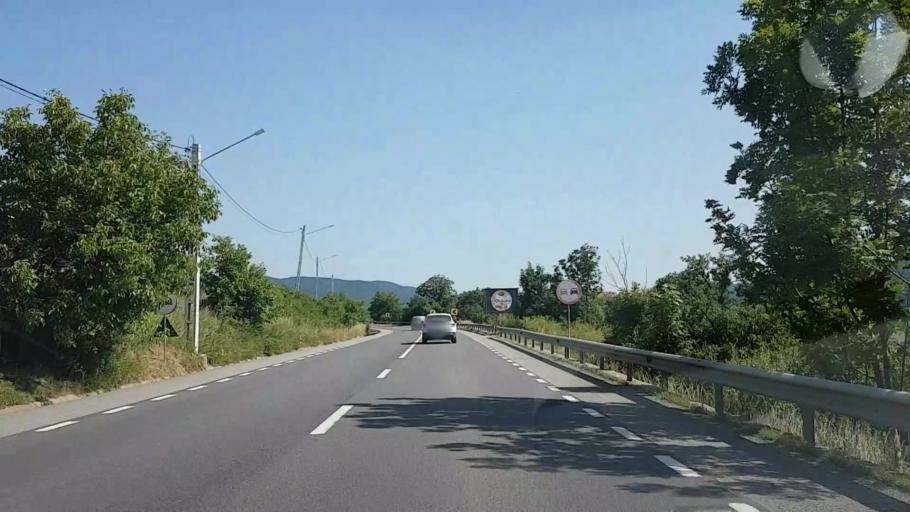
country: RO
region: Bistrita-Nasaud
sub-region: Comuna Sieu-Magherus
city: Sieu-Magherus
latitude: 47.0750
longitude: 24.3988
